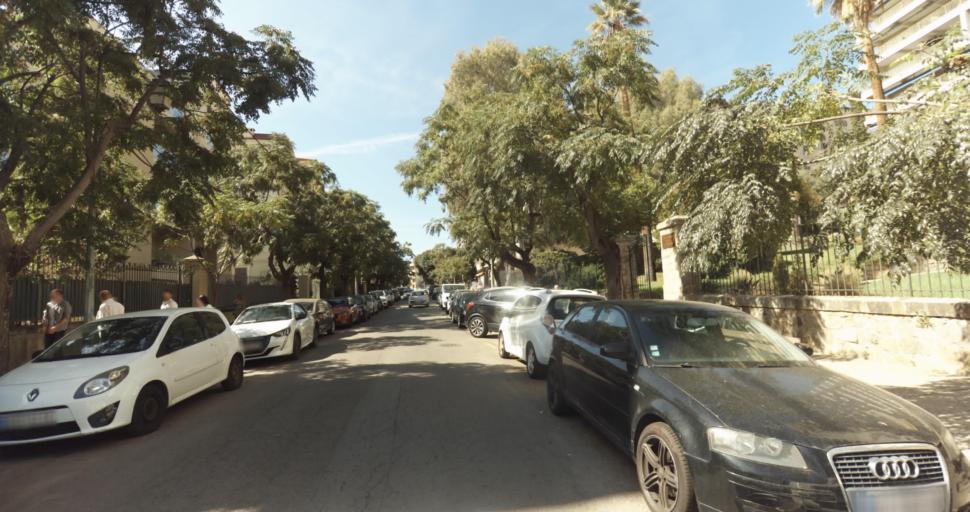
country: FR
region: Corsica
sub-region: Departement de la Corse-du-Sud
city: Ajaccio
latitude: 41.9161
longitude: 8.7289
